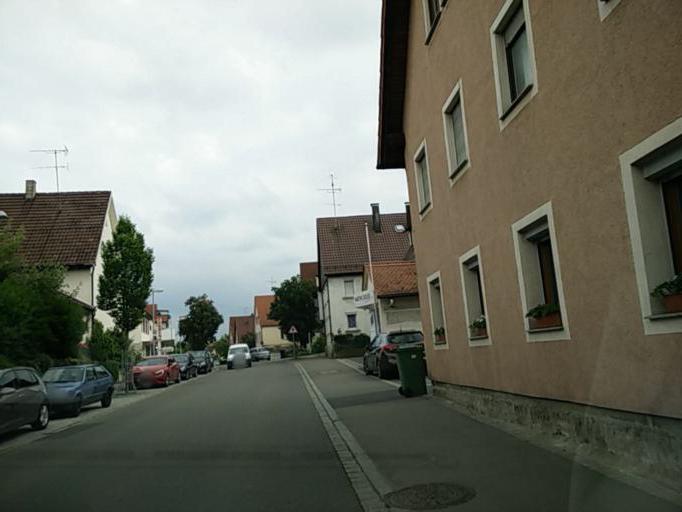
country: DE
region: Baden-Wuerttemberg
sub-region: Regierungsbezirk Stuttgart
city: Holzgerlingen
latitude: 48.6354
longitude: 9.0126
